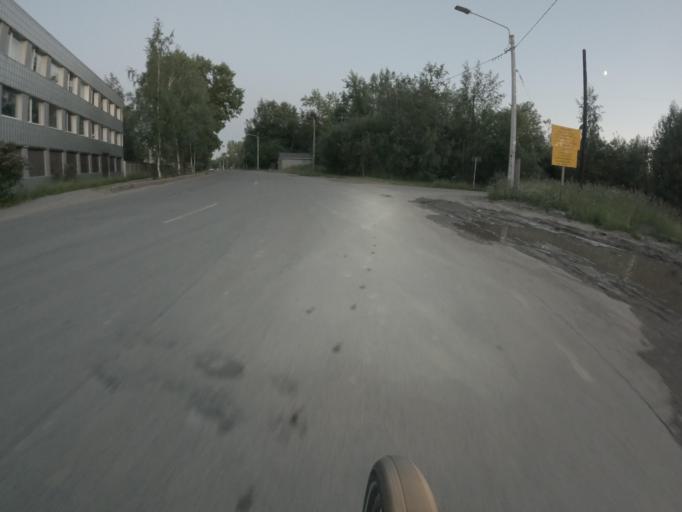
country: RU
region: St.-Petersburg
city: Sapernyy
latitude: 59.7770
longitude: 30.6894
